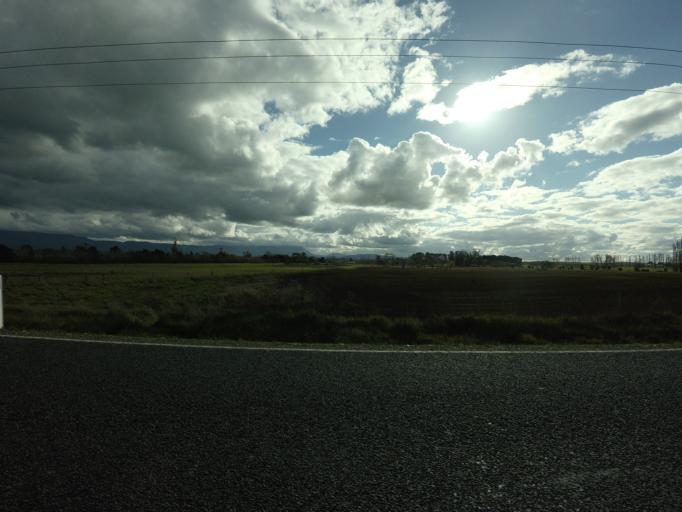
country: AU
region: Tasmania
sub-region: Northern Midlands
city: Longford
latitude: -41.7226
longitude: 147.0898
